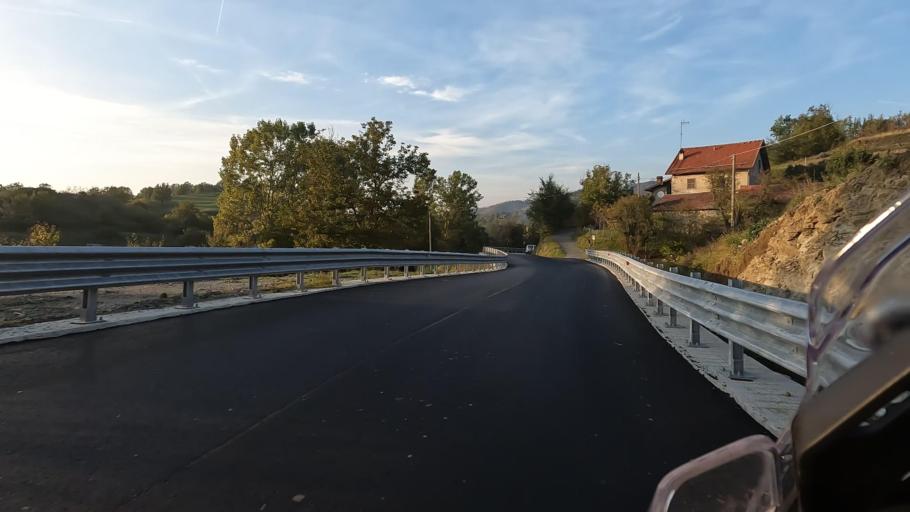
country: IT
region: Liguria
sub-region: Provincia di Savona
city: Sassello
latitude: 44.4939
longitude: 8.4966
